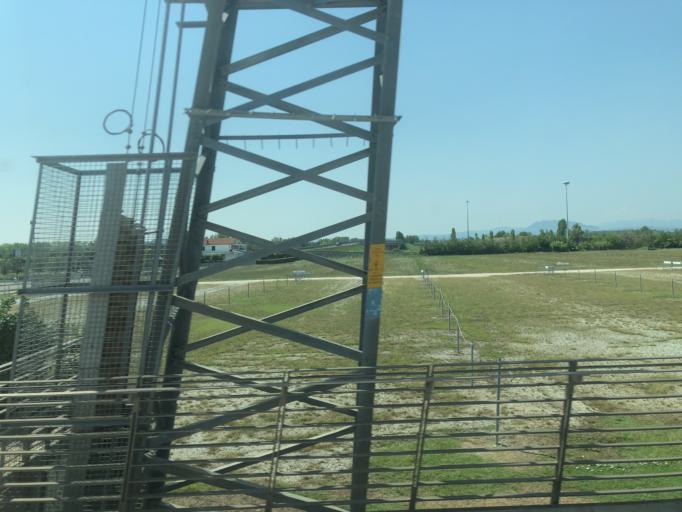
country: IT
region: Emilia-Romagna
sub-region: Provincia di Rimini
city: Santa Giustina
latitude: 44.0707
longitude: 12.5252
